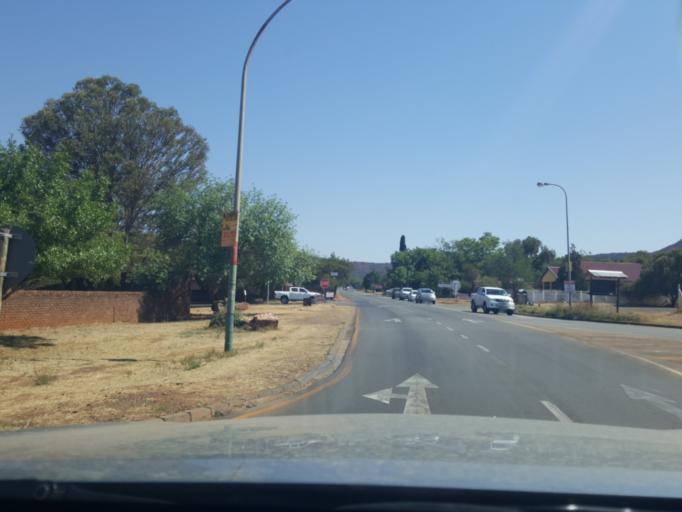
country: ZA
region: North-West
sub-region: Ngaka Modiri Molema District Municipality
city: Zeerust
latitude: -25.5373
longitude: 26.0772
